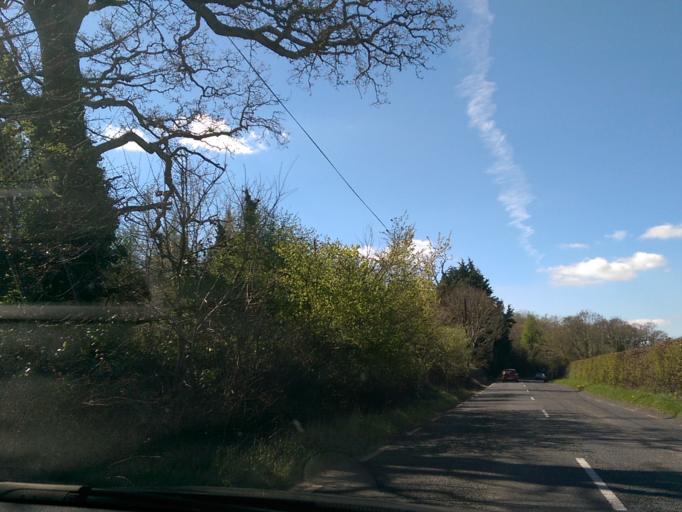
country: IE
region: Leinster
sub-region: Laois
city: Stradbally
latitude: 53.0177
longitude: -7.0942
